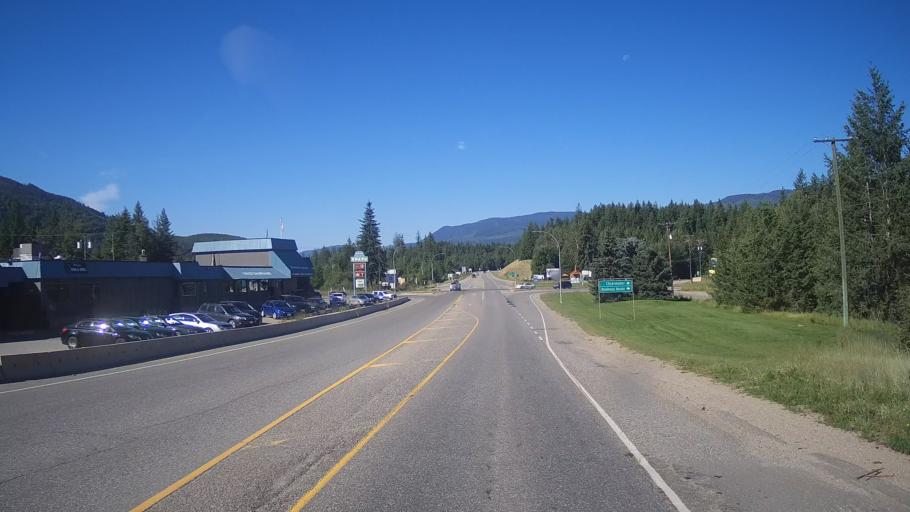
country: CA
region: British Columbia
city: Chase
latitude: 51.6481
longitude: -120.0492
